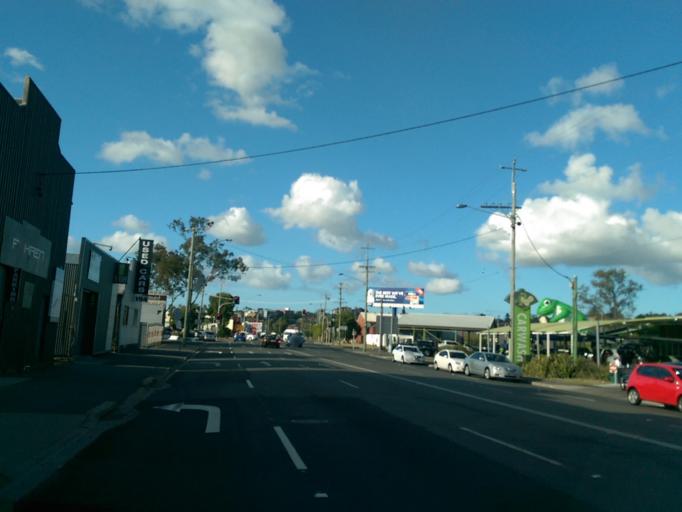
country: AU
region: Queensland
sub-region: Brisbane
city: Windsor
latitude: -27.4377
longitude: 153.0409
